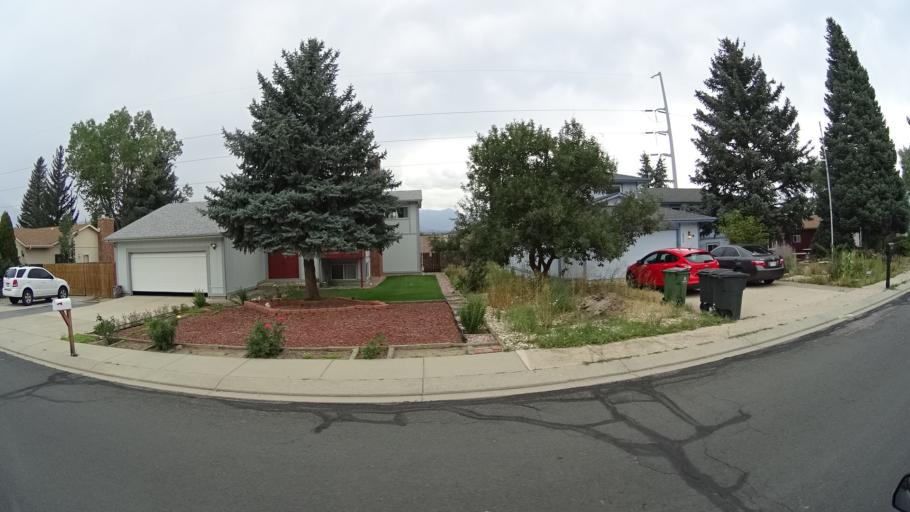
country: US
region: Colorado
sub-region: El Paso County
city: Air Force Academy
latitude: 38.9227
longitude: -104.8123
